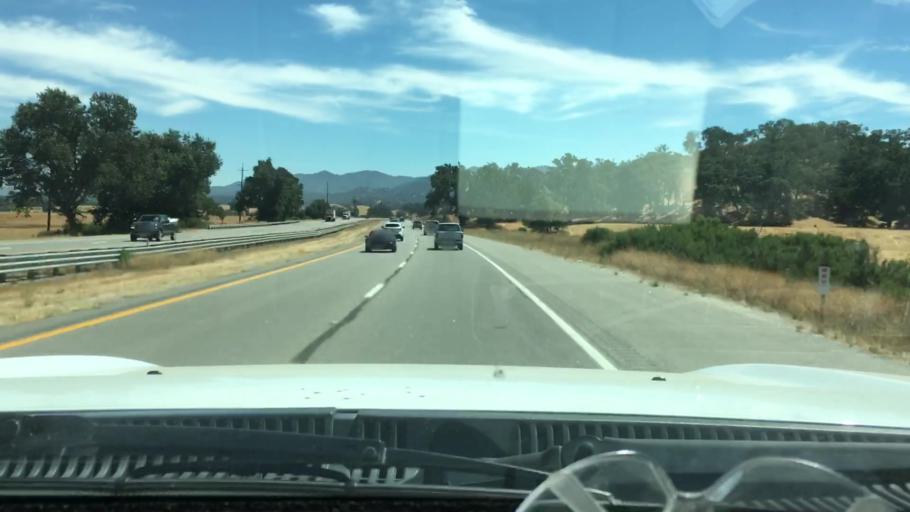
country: US
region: California
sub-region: San Luis Obispo County
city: Santa Margarita
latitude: 35.4087
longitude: -120.6263
